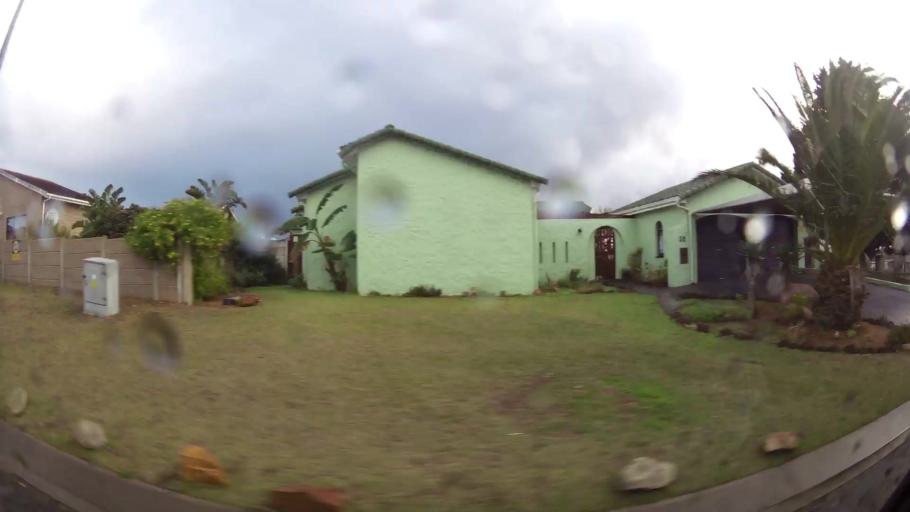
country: ZA
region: Western Cape
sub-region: Eden District Municipality
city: Mossel Bay
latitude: -34.1896
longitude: 22.1080
